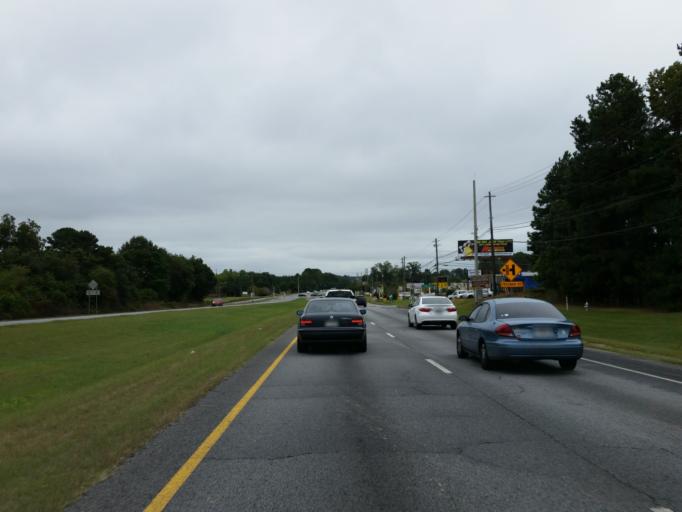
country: US
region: Georgia
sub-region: Clayton County
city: Bonanza
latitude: 33.4794
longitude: -84.3385
